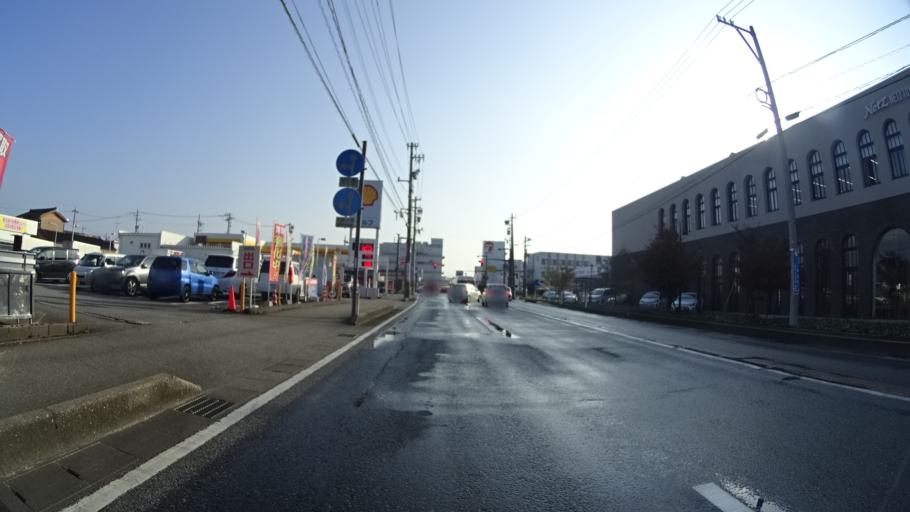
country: JP
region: Toyama
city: Toyama-shi
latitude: 36.7035
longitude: 137.2590
